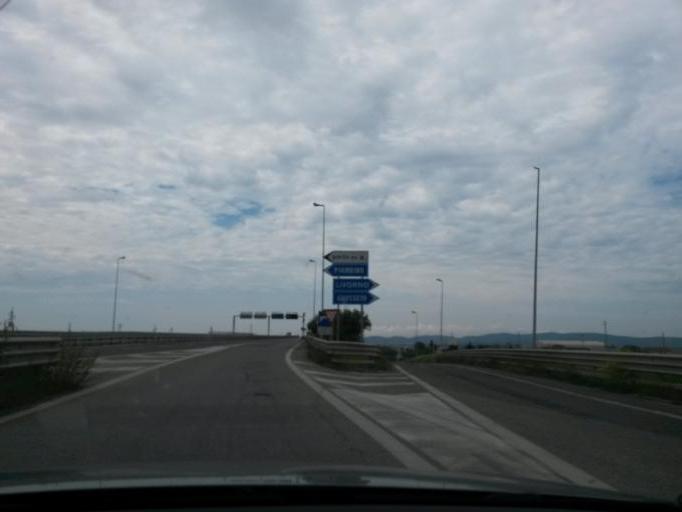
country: IT
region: Tuscany
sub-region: Provincia di Livorno
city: Venturina
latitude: 43.0156
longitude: 10.5976
